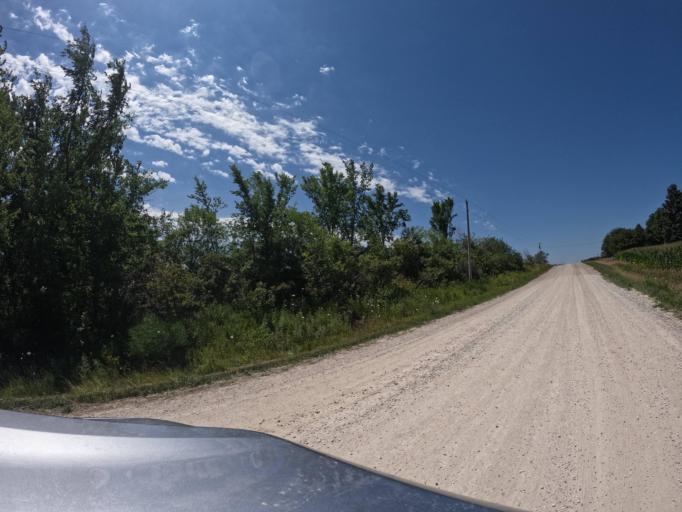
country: US
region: Iowa
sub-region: Keokuk County
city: Sigourney
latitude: 41.4668
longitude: -92.3555
